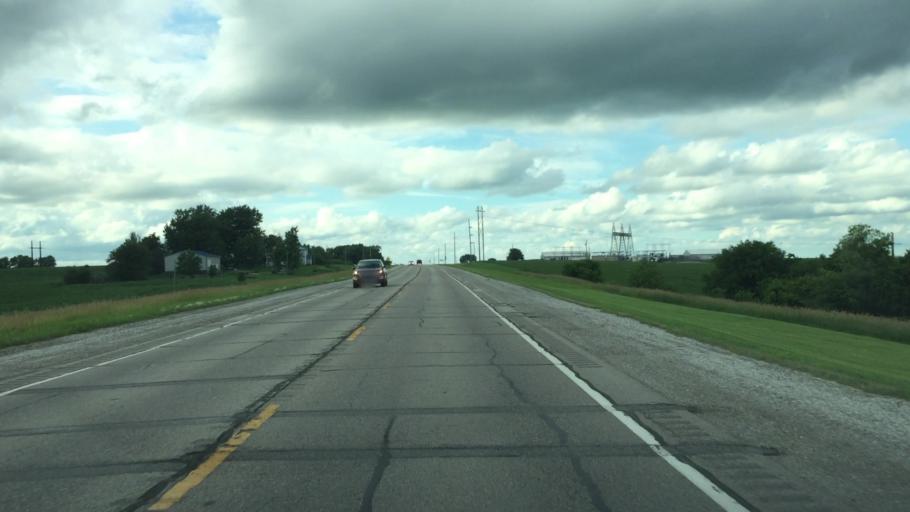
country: US
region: Iowa
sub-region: Jasper County
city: Monroe
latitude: 41.5688
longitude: -93.0969
